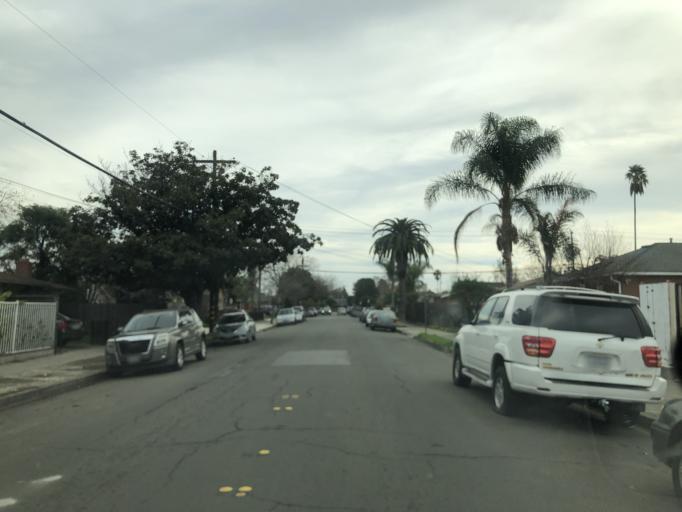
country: US
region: California
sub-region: Santa Clara County
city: Alum Rock
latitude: 37.3494
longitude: -121.8577
